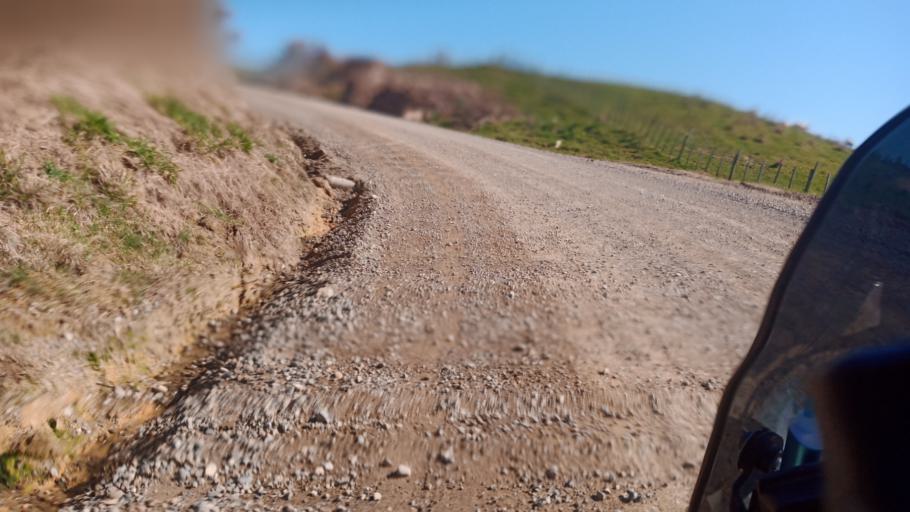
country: NZ
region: Gisborne
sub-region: Gisborne District
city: Gisborne
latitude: -39.1136
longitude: 177.9625
